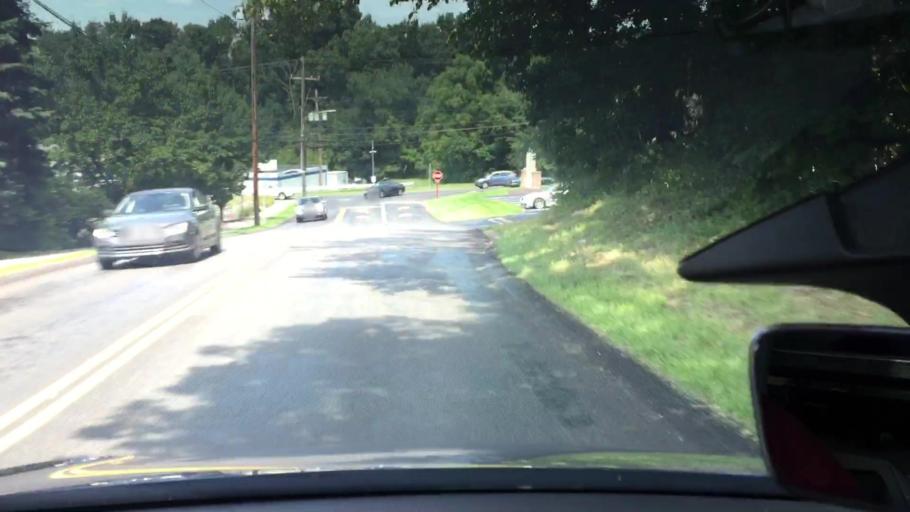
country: US
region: Pennsylvania
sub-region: Allegheny County
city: Monroeville
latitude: 40.4407
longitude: -79.7749
